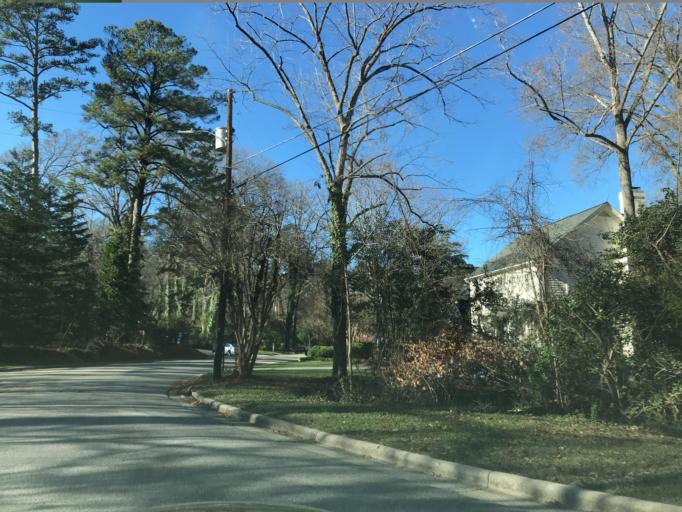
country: US
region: North Carolina
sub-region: Wake County
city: West Raleigh
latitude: 35.8192
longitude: -78.6446
